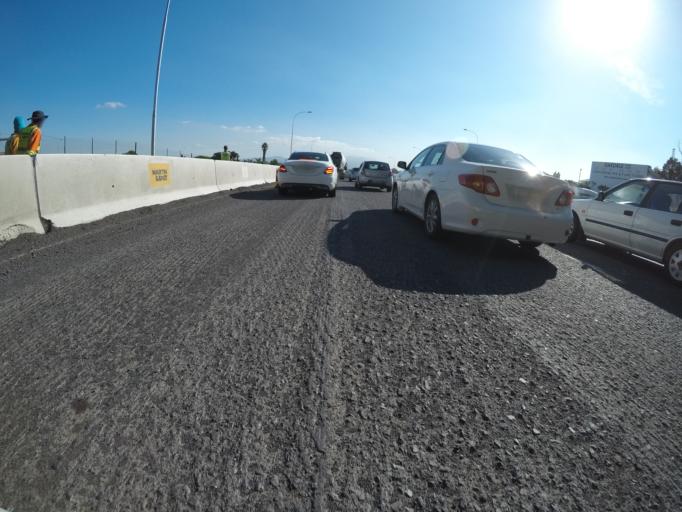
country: ZA
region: Western Cape
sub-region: City of Cape Town
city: Kraaifontein
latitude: -33.8824
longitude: 18.6462
